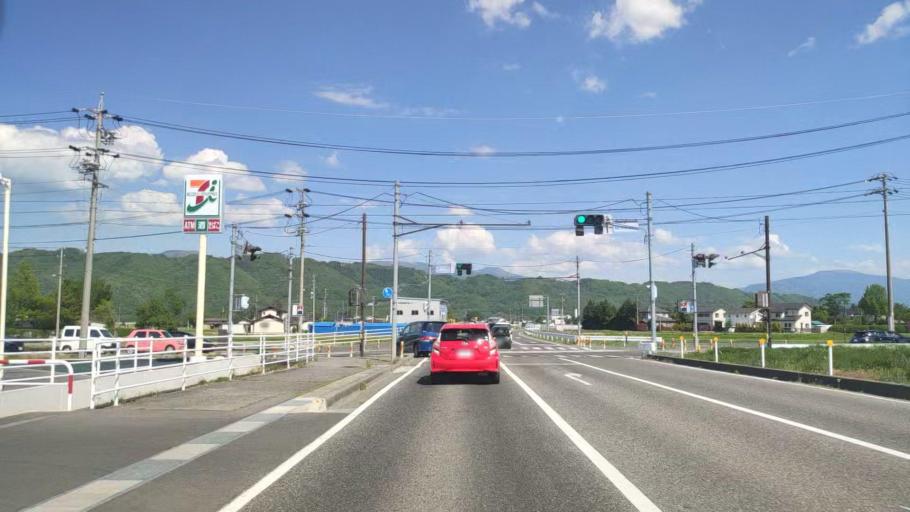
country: JP
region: Nagano
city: Toyoshina
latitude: 36.2799
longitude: 137.9204
